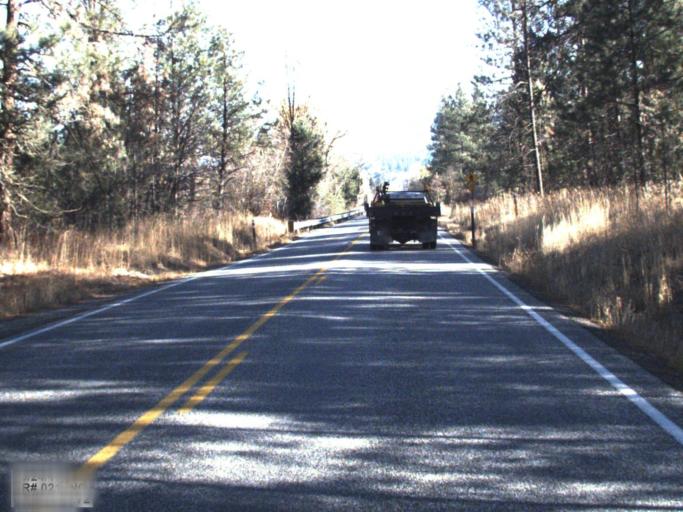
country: US
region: Washington
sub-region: Ferry County
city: Republic
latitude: 48.7978
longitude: -118.6146
